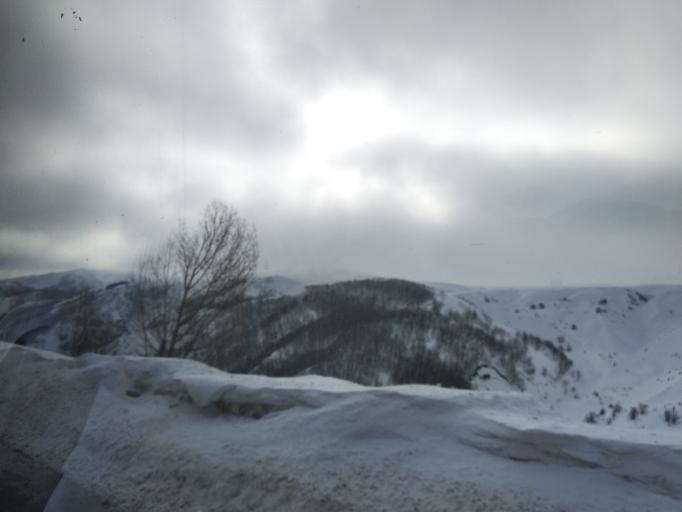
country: TR
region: Erzincan
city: Catalarmut
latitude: 39.8935
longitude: 39.3752
